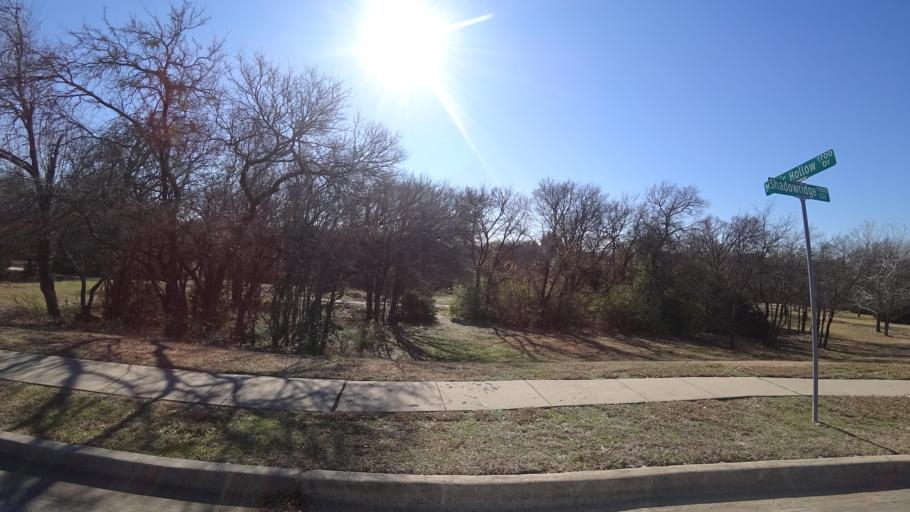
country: US
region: Texas
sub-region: Denton County
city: Lewisville
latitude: 33.0237
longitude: -97.0215
